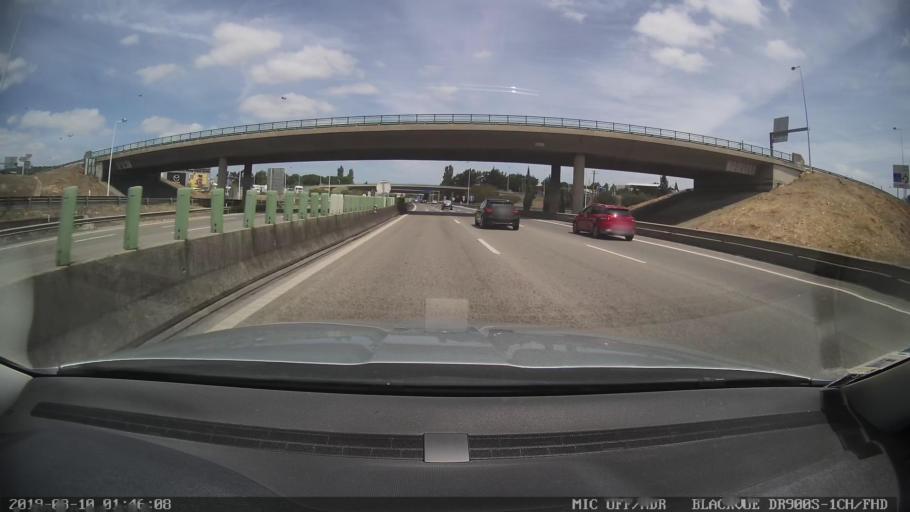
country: PT
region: Lisbon
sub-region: Vila Franca de Xira
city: Vialonga
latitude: 38.8914
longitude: -9.0525
